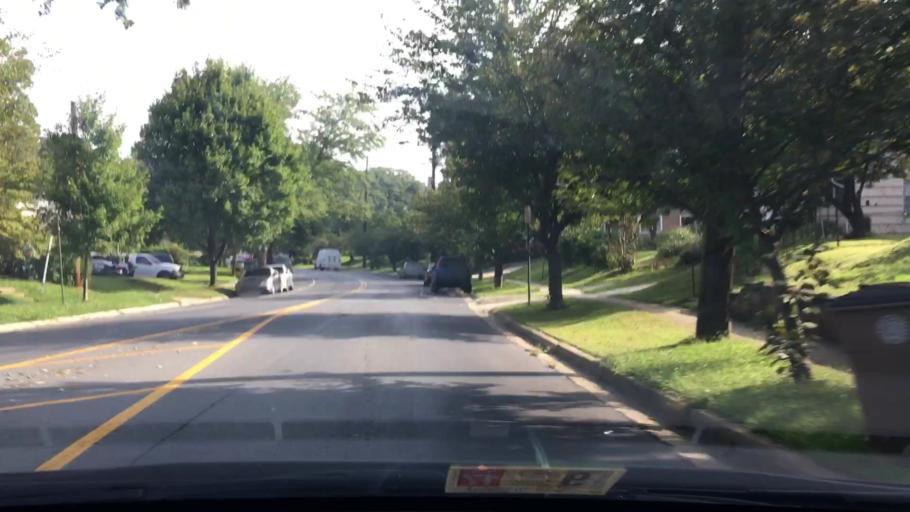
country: US
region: Maryland
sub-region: Montgomery County
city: Rockville
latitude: 39.0762
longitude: -77.1318
